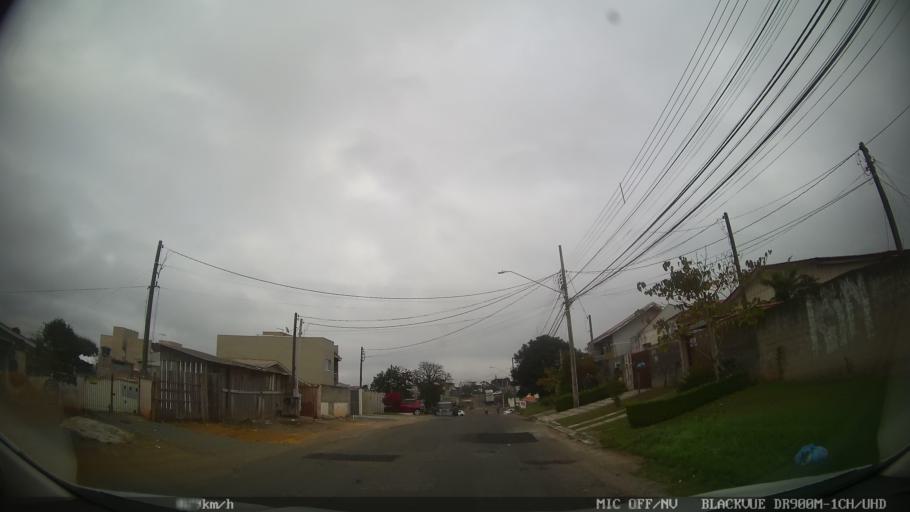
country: BR
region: Parana
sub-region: Almirante Tamandare
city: Almirante Tamandare
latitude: -25.3790
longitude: -49.3327
